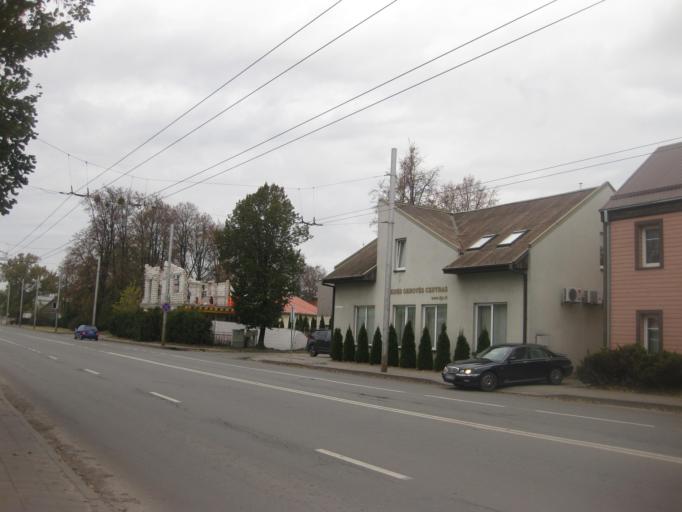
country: LT
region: Kauno apskritis
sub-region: Kaunas
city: Eiguliai
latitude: 54.9095
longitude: 23.9276
